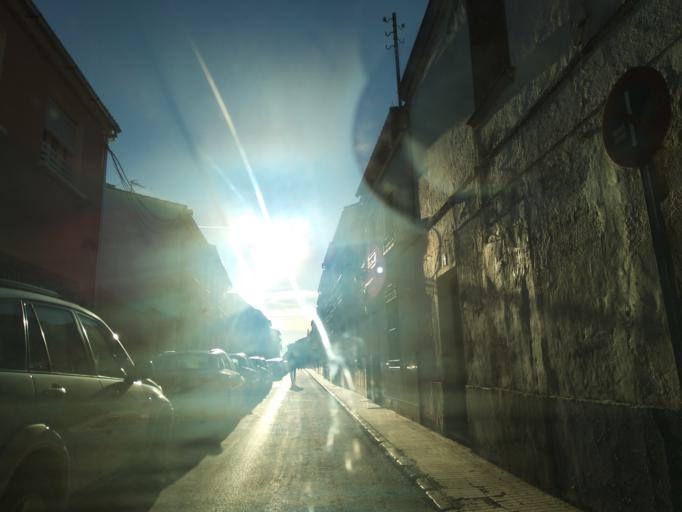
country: ES
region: Andalusia
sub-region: Provincia de Malaga
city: Campillos
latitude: 37.0503
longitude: -4.8644
